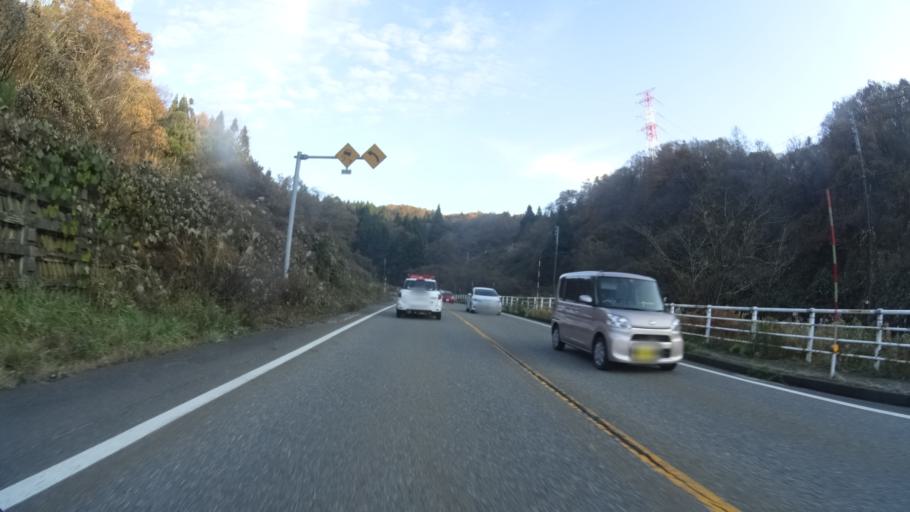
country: JP
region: Niigata
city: Kashiwazaki
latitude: 37.4054
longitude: 138.6892
